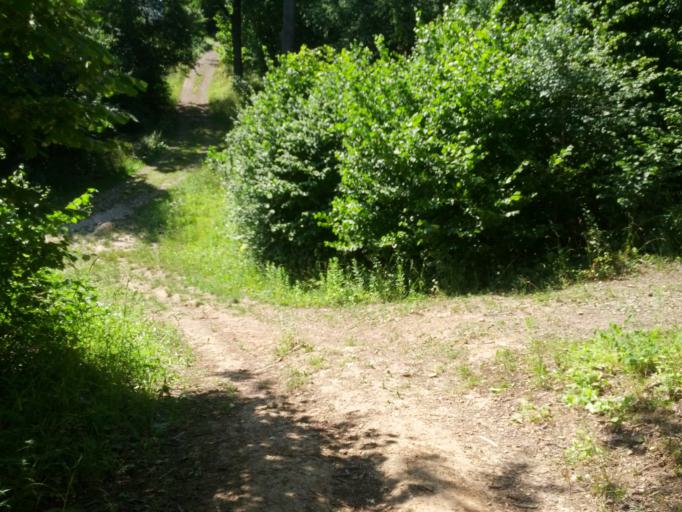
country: DE
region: Thuringia
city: Krauthausen
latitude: 50.9876
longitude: 10.2774
